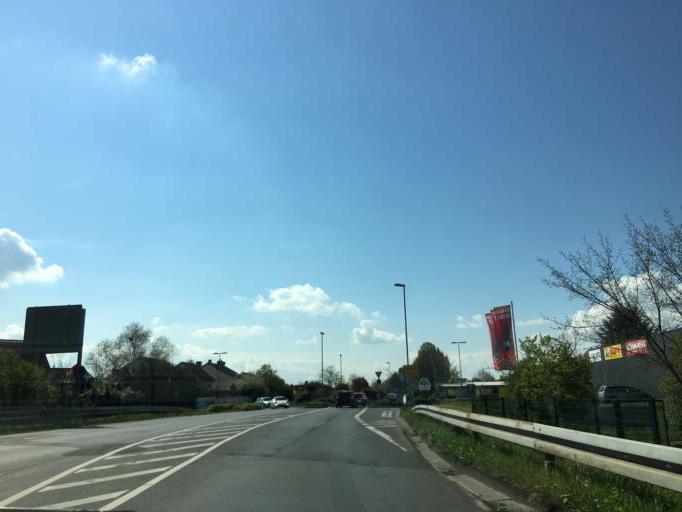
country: DE
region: Hesse
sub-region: Regierungsbezirk Darmstadt
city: Rodgau
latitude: 50.0153
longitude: 8.8907
